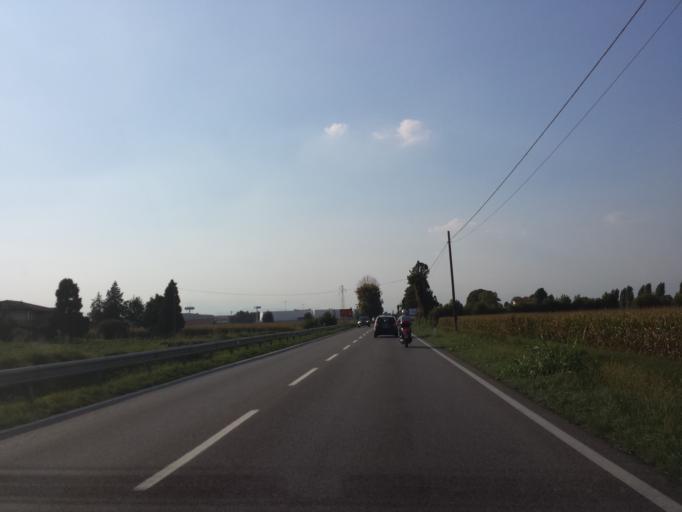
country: IT
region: Veneto
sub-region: Provincia di Vicenza
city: Torri di Quartesolo
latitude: 45.5045
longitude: 11.6385
